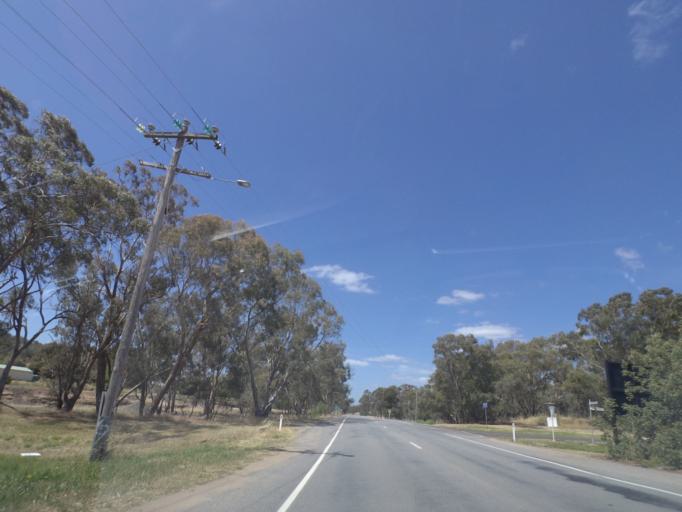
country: AU
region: Victoria
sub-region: Wangaratta
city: Wangaratta
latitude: -36.4631
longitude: 146.2271
